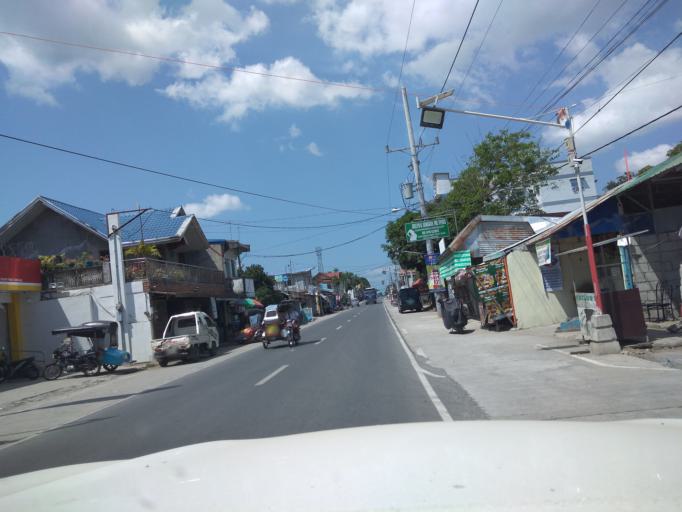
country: PH
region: Central Luzon
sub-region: Province of Pampanga
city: Bahay Pare
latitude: 15.0289
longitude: 120.8821
